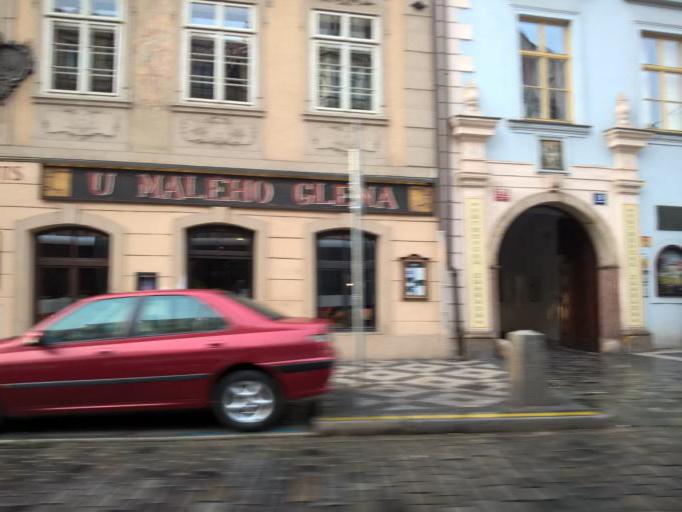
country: CZ
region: Praha
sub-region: Praha 1
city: Mala Strana
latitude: 50.0869
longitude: 14.4038
